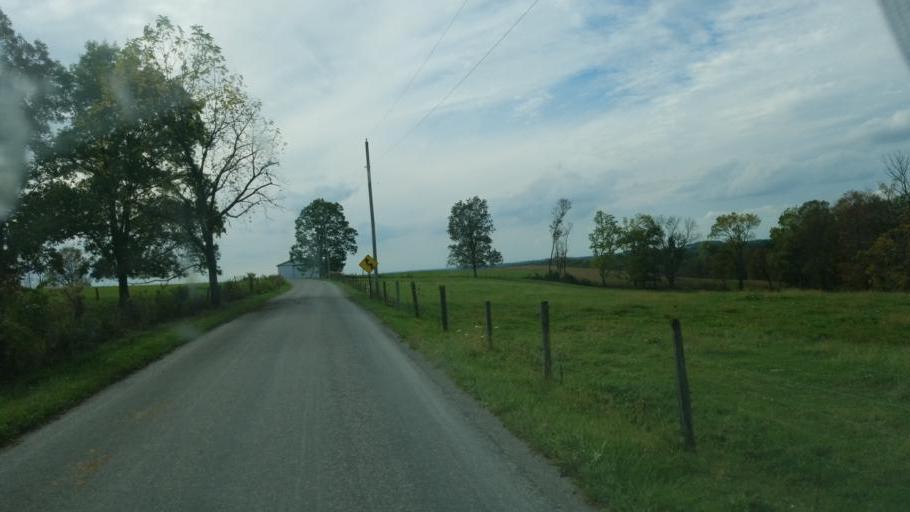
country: US
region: Ohio
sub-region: Holmes County
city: Millersburg
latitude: 40.6082
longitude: -81.7883
